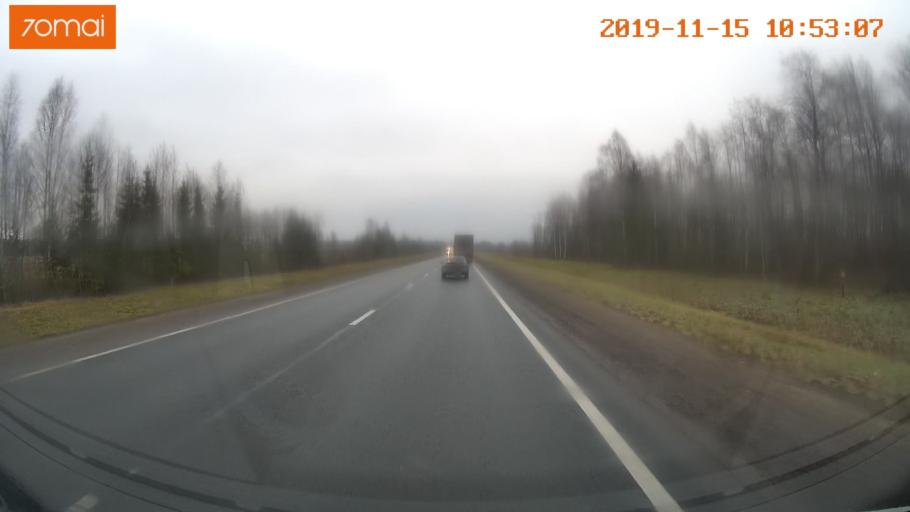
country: RU
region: Vologda
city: Chebsara
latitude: 59.1707
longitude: 38.7476
